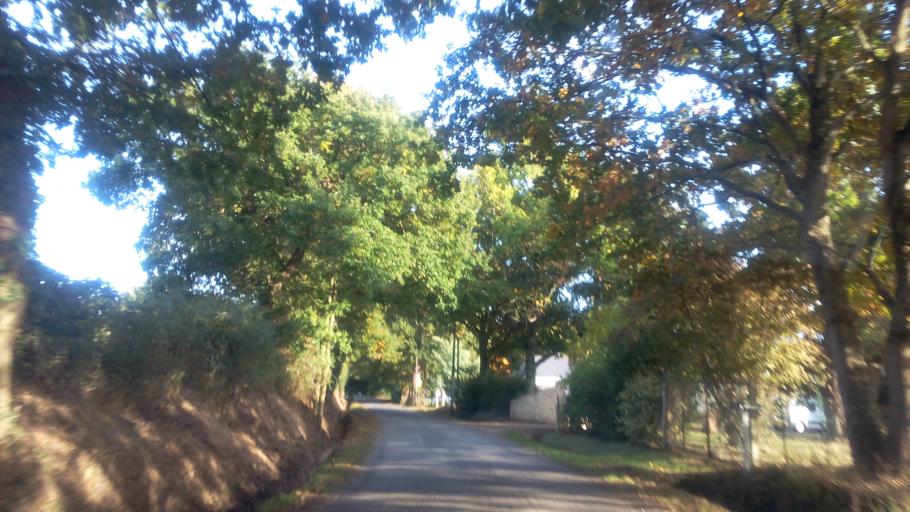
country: FR
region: Brittany
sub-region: Departement du Morbihan
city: Saint-Perreux
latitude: 47.6980
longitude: -2.1125
